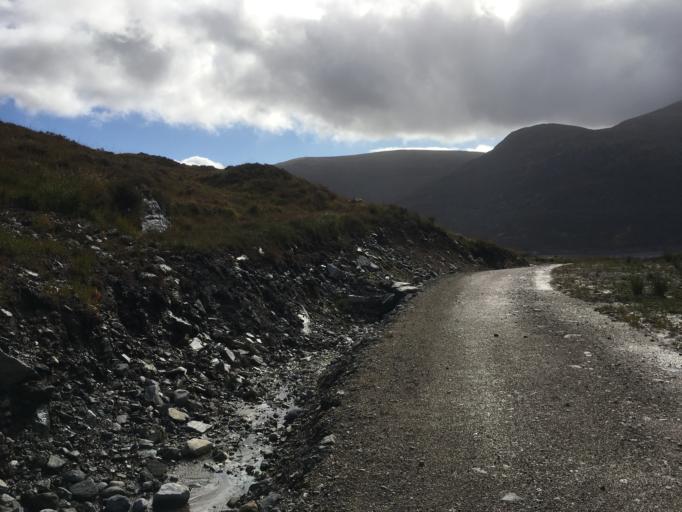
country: GB
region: Scotland
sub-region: Highland
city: Spean Bridge
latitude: 57.3465
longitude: -4.9821
